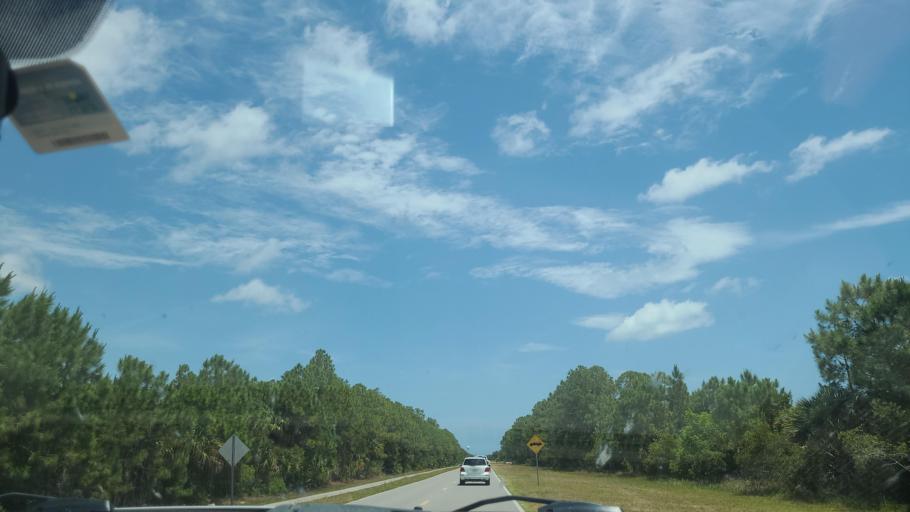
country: US
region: Florida
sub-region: Brevard County
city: Grant-Valkaria
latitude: 27.9593
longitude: -80.5679
